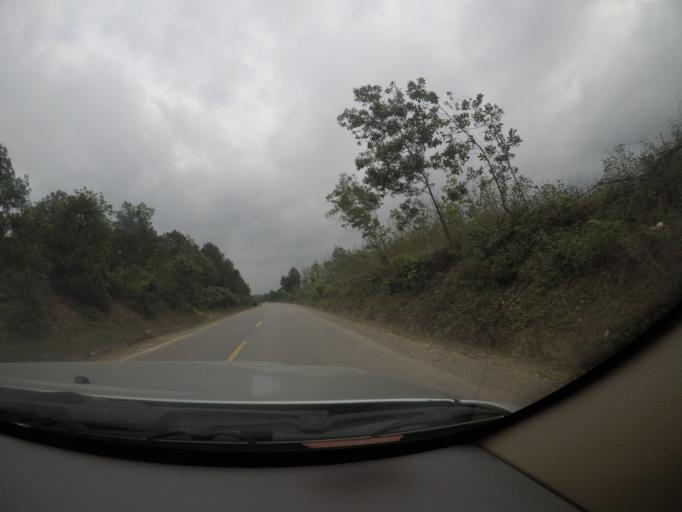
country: VN
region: Quang Binh
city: Kien Giang
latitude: 17.1715
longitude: 106.7389
